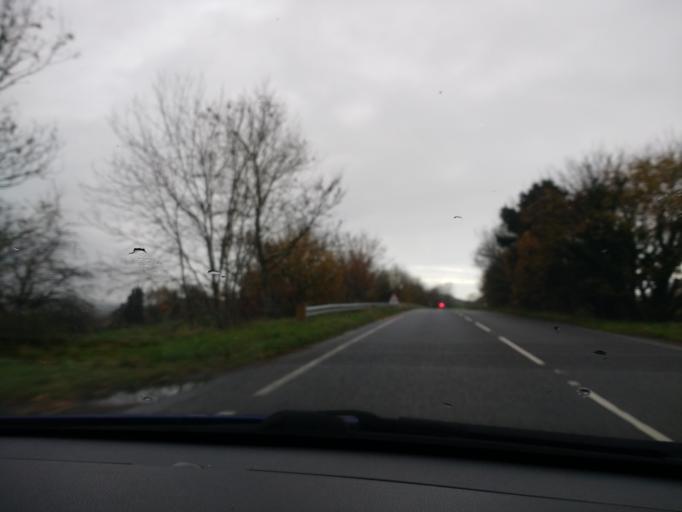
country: GB
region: England
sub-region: Cumbria
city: Millom
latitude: 54.2709
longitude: -3.2505
